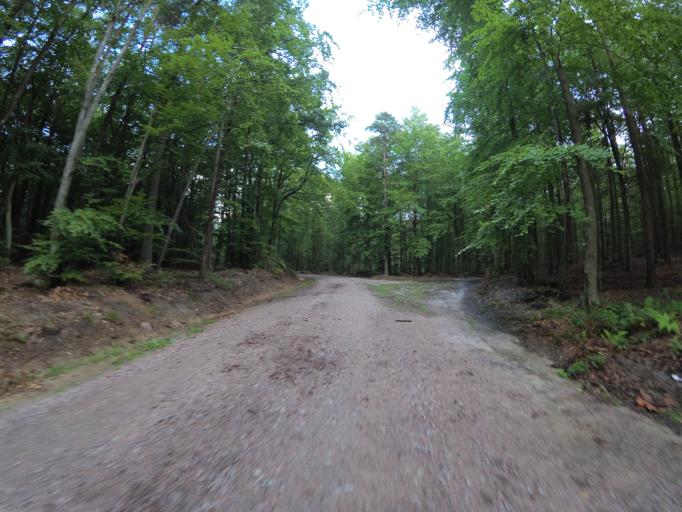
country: PL
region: Pomeranian Voivodeship
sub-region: Powiat wejherowski
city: Bojano
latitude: 54.5089
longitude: 18.4202
